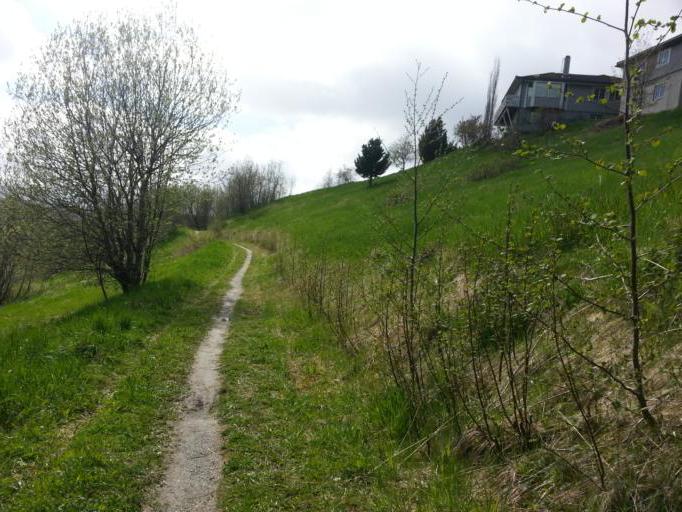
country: NO
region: Sor-Trondelag
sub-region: Trondheim
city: Trondheim
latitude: 63.3877
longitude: 10.3673
